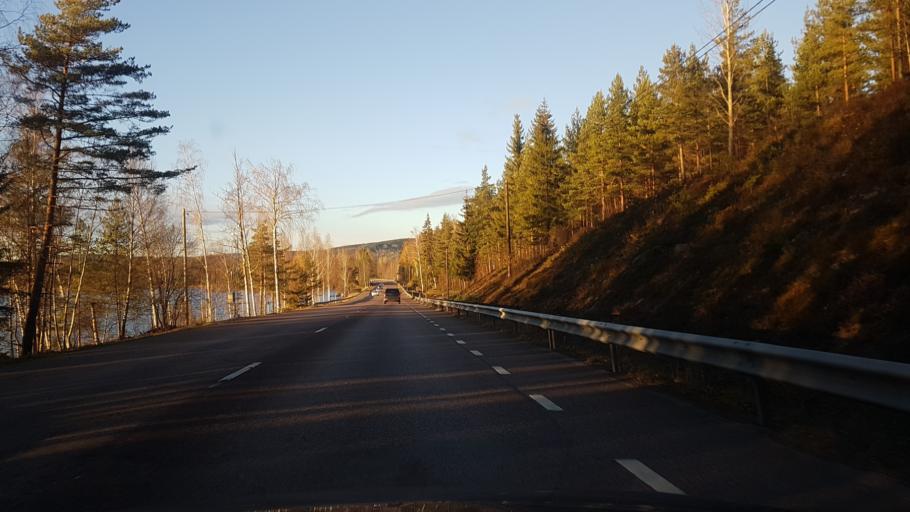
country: SE
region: Dalarna
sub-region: Faluns Kommun
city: Bjursas
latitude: 60.7131
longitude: 15.4611
